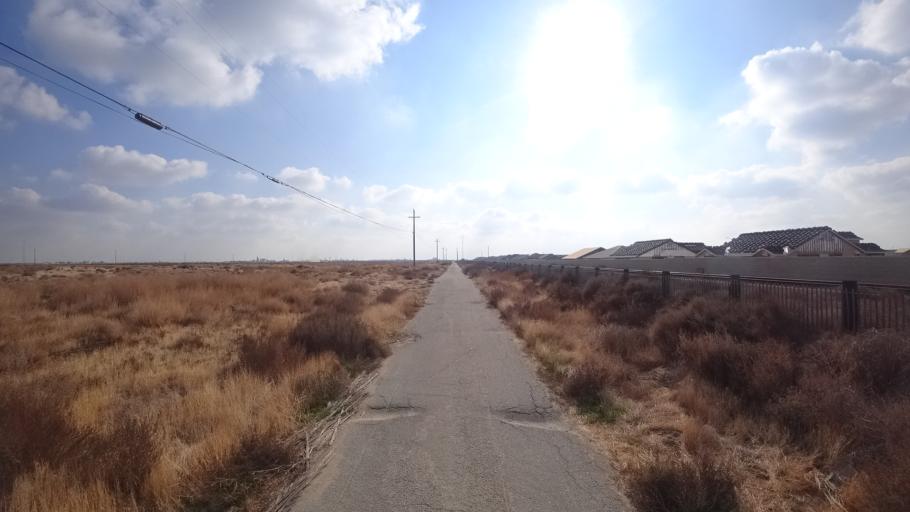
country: US
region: California
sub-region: Kern County
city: Greenacres
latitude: 35.2922
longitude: -119.1010
